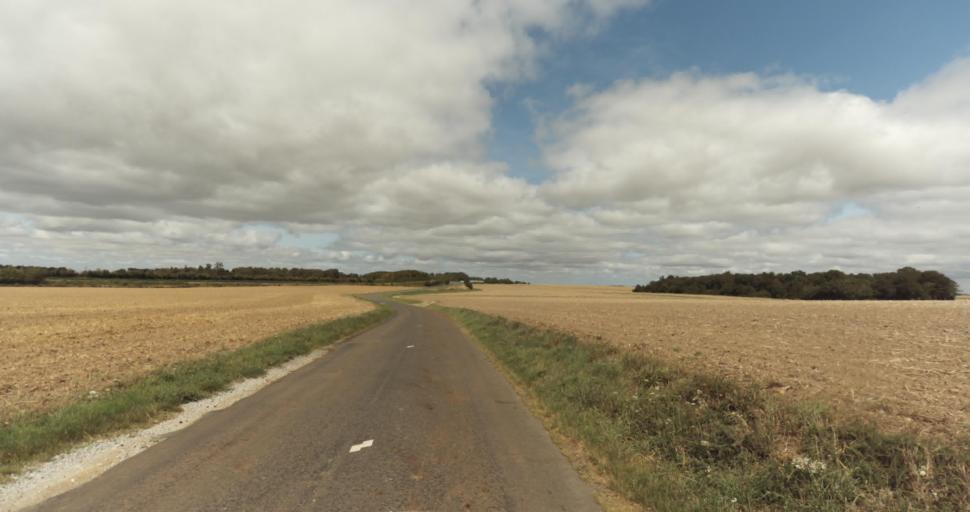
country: FR
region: Haute-Normandie
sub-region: Departement de l'Eure
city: Evreux
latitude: 48.9211
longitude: 1.2060
